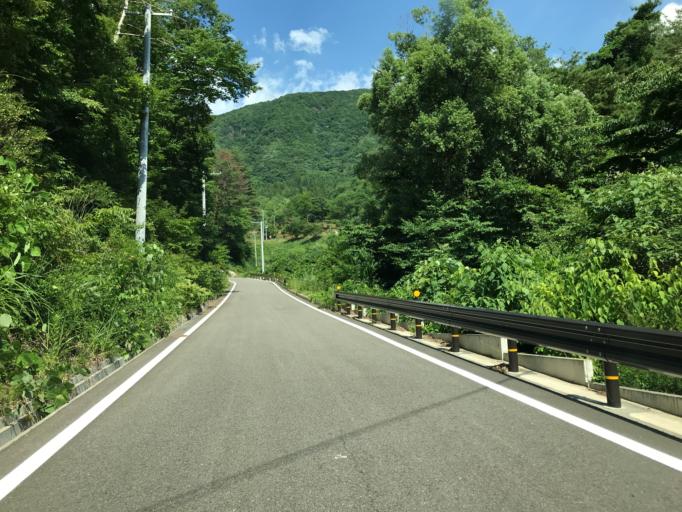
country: JP
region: Fukushima
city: Yanagawamachi-saiwaicho
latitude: 37.7839
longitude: 140.6669
